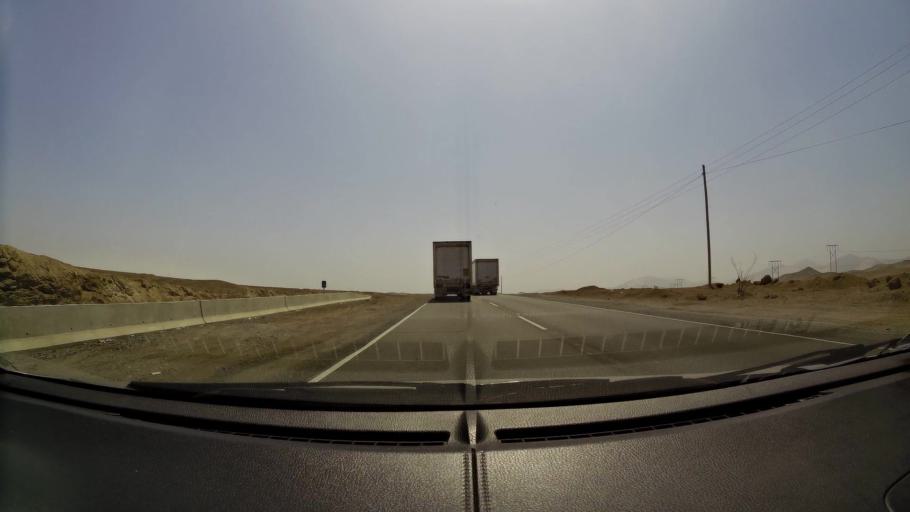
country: PE
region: Ancash
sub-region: Provincia de Huarmey
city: Huarmey
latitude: -10.1850
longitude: -78.0669
